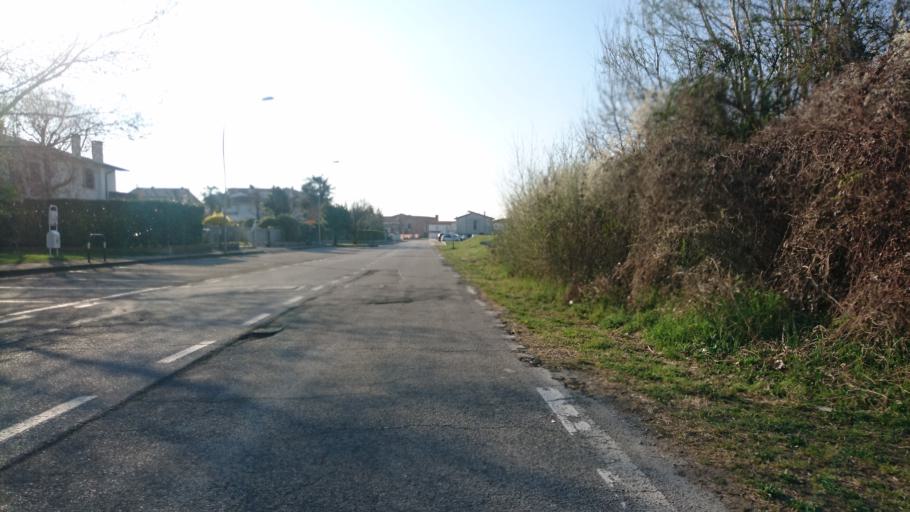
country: IT
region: Veneto
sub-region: Provincia di Padova
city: Vigonza
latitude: 45.4422
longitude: 11.9863
